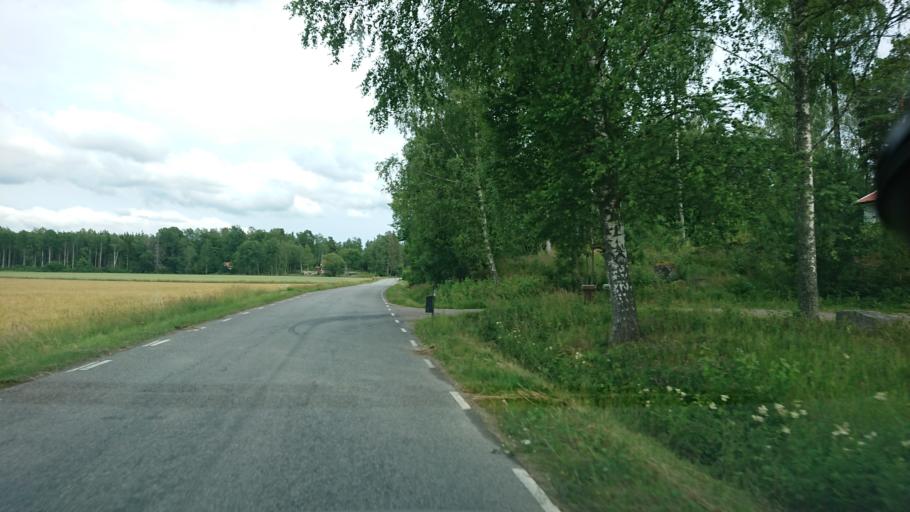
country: SE
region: Uppsala
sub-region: Osthammars Kommun
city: Bjorklinge
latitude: 60.0010
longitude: 17.4677
